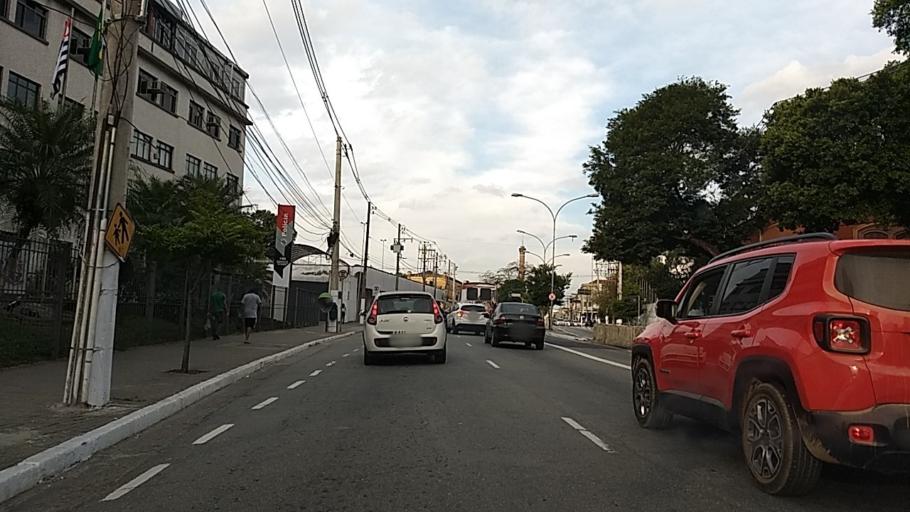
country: BR
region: Sao Paulo
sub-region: Sao Paulo
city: Sao Paulo
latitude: -23.5320
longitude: -46.6341
